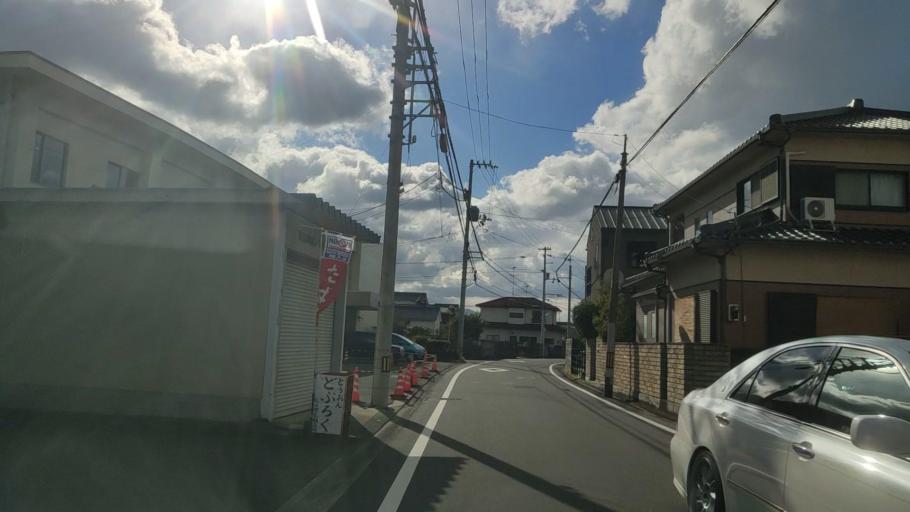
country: JP
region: Ehime
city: Masaki-cho
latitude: 33.8269
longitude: 132.7087
